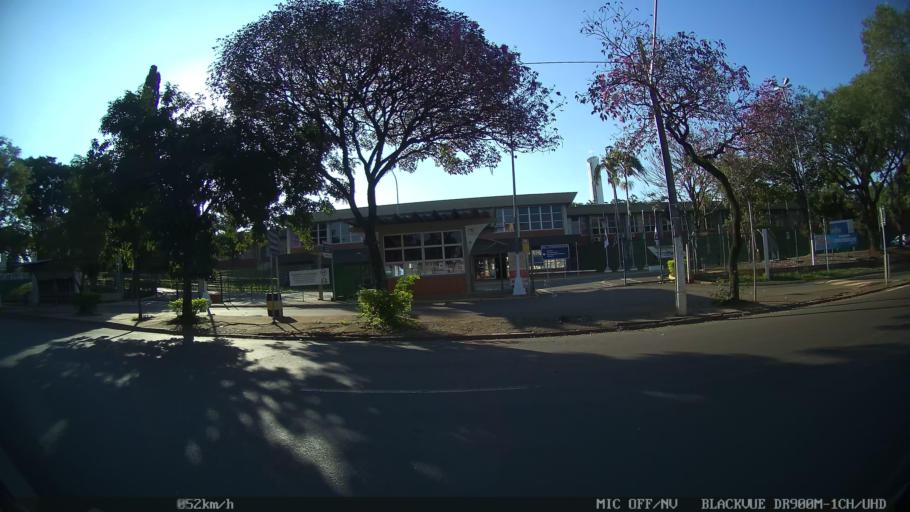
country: BR
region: Sao Paulo
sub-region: Piracicaba
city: Piracicaba
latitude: -22.7024
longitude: -47.6474
